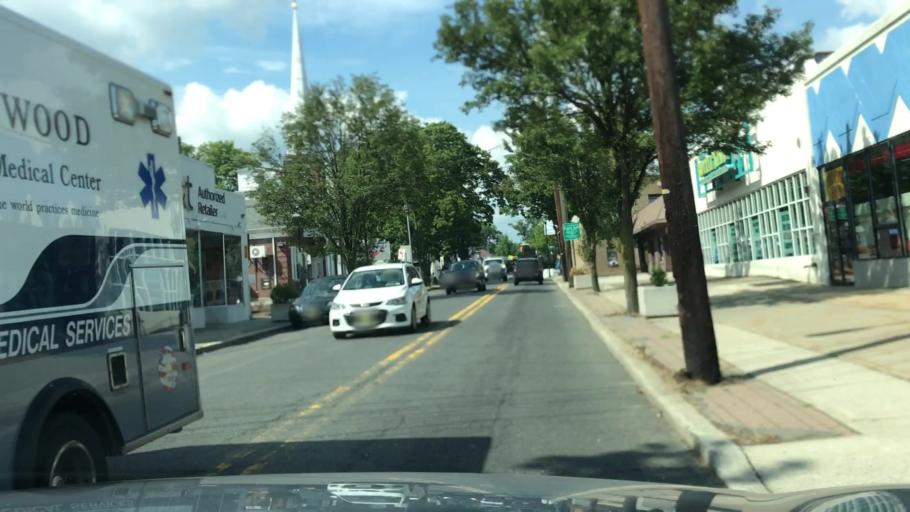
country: US
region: New Jersey
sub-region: Bergen County
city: Dumont
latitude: 40.9392
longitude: -73.9941
